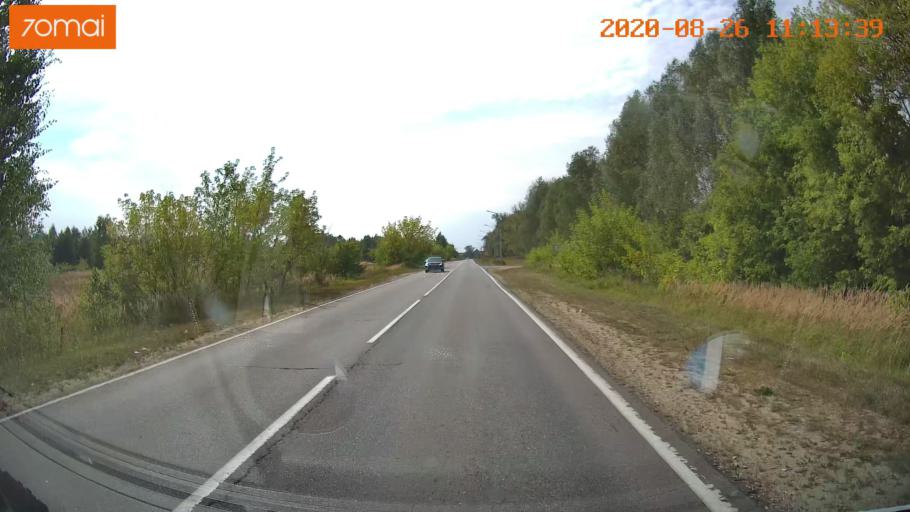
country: RU
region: Rjazan
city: Izhevskoye
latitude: 54.4547
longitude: 41.1193
